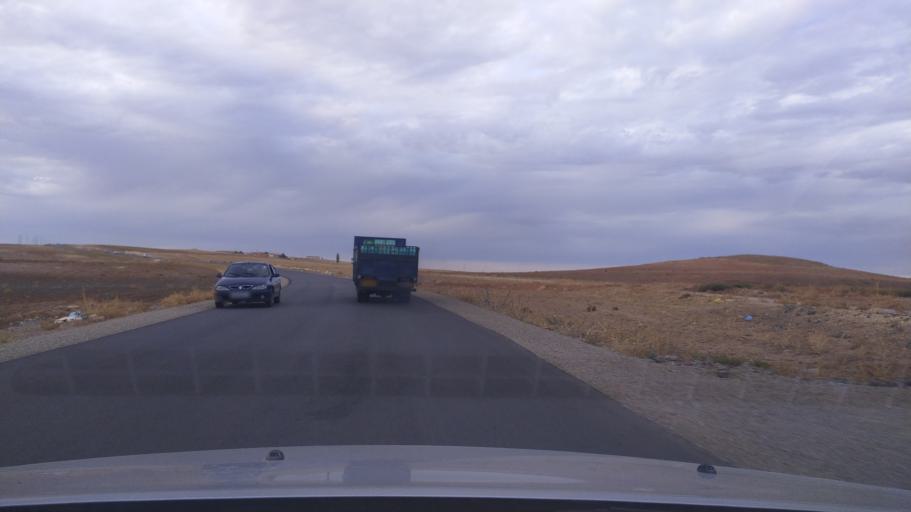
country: DZ
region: Tiaret
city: Frenda
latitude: 34.9980
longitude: 1.1277
